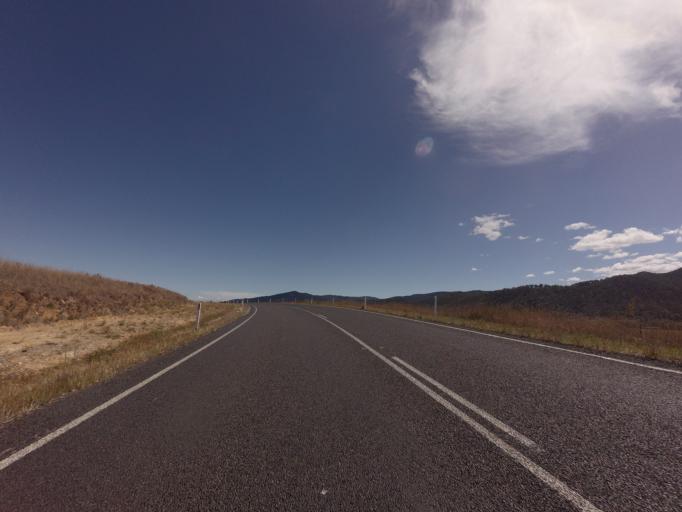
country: AU
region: Tasmania
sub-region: Break O'Day
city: St Helens
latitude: -41.7027
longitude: 147.8510
